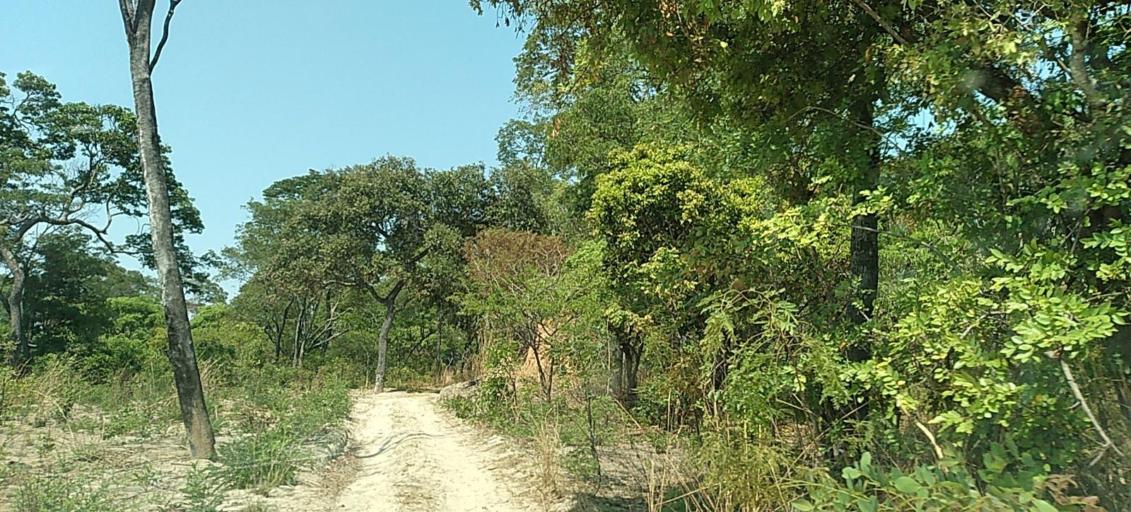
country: ZM
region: Copperbelt
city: Mpongwe
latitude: -13.7914
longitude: 28.0919
